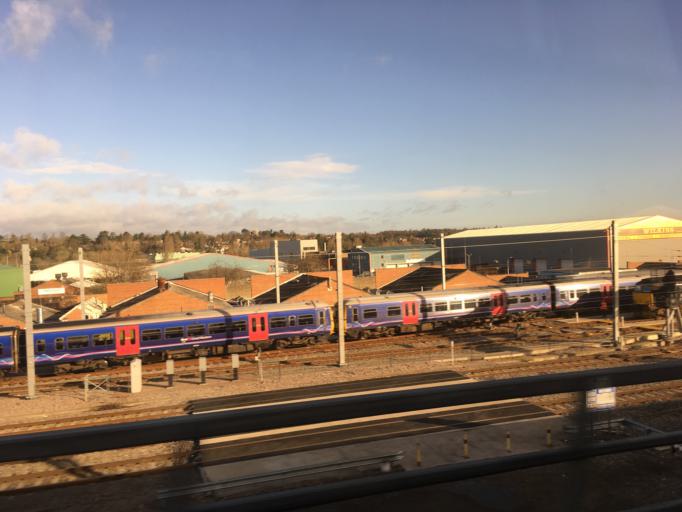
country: GB
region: England
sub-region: Reading
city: Reading
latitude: 51.4607
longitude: -0.9867
